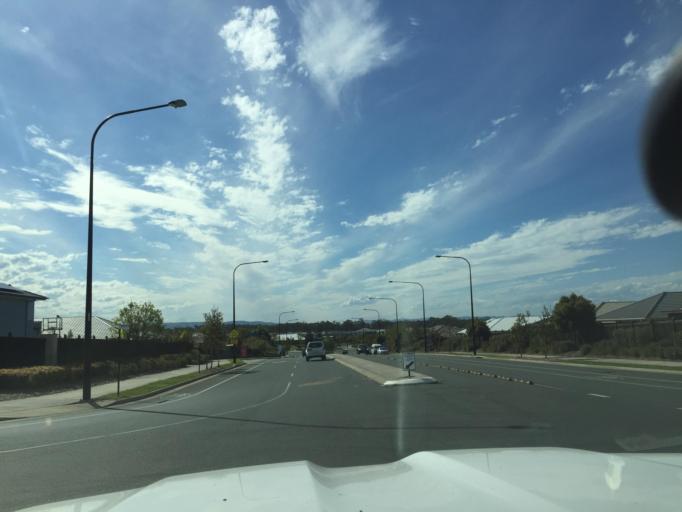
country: AU
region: Queensland
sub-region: Moreton Bay
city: Morayfield
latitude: -27.1213
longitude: 152.9963
